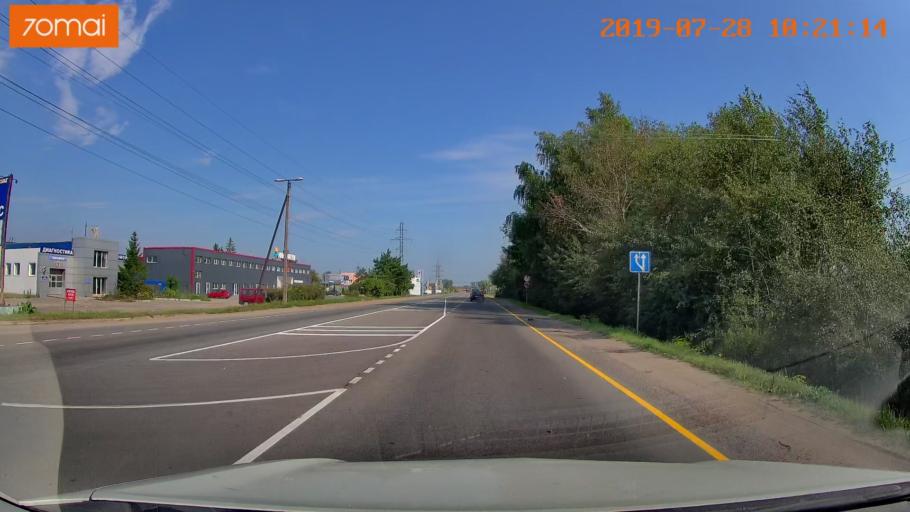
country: RU
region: Kaliningrad
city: Maloye Isakovo
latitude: 54.7556
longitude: 20.5648
